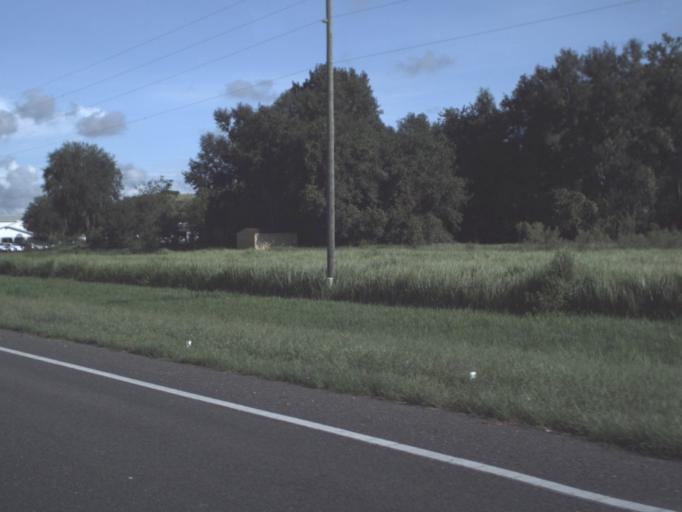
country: US
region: Florida
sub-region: Polk County
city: Fort Meade
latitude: 27.7866
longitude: -81.8105
